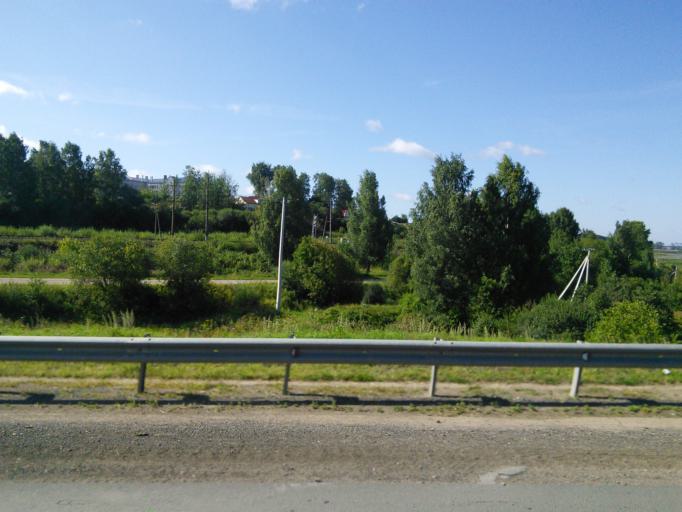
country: RU
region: Vologda
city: Sheksna
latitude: 59.2104
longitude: 38.4994
